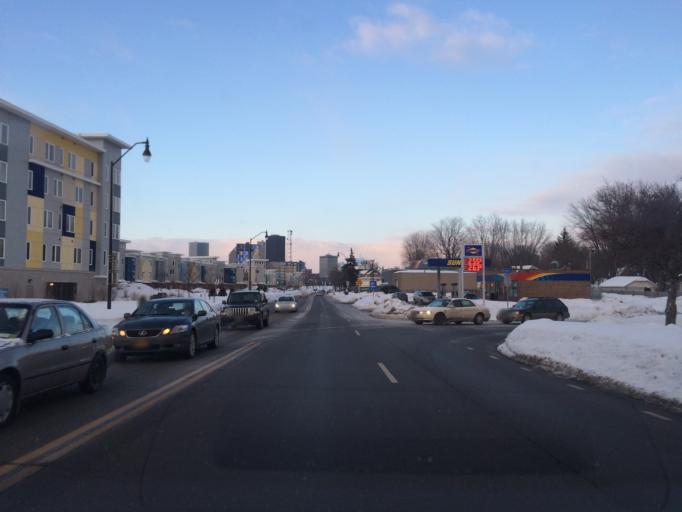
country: US
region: New York
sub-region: Monroe County
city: Rochester
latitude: 43.1415
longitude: -77.6130
